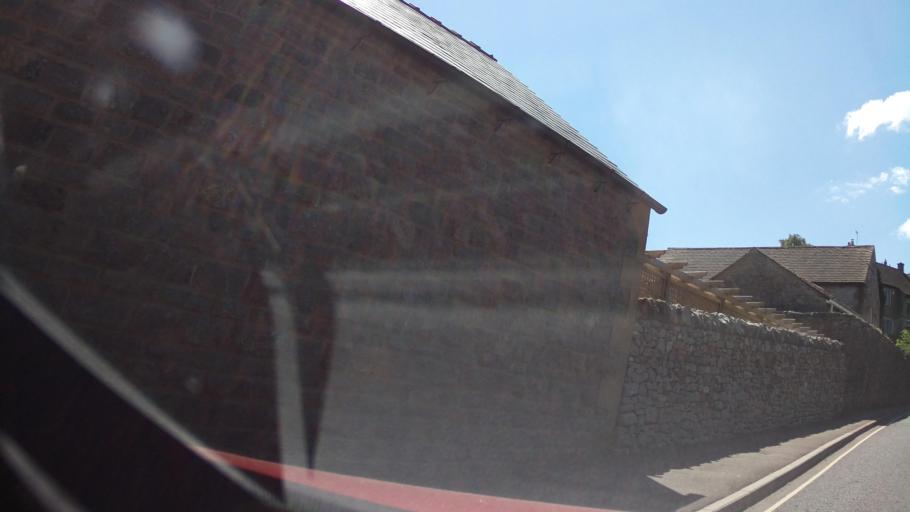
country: GB
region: England
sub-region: Derbyshire
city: Bakewell
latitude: 53.2116
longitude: -1.6830
